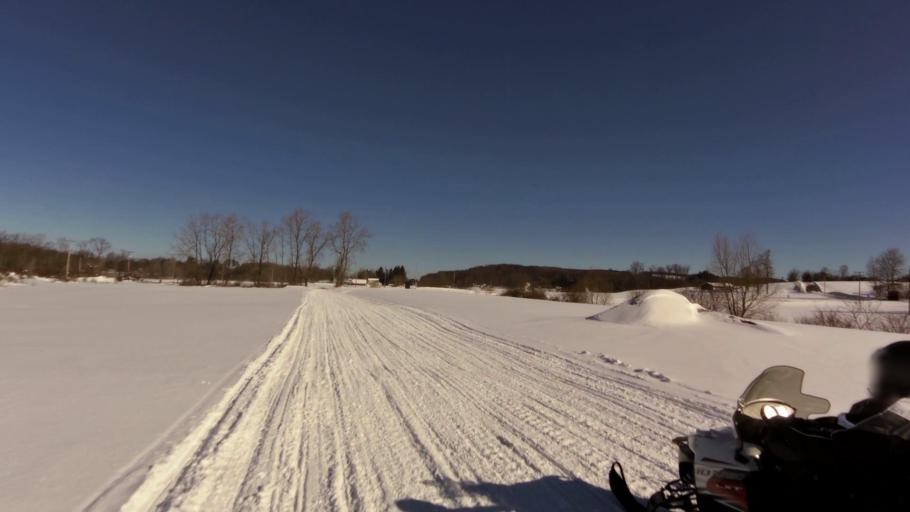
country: US
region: New York
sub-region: Cattaraugus County
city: Franklinville
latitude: 42.4015
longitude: -78.4740
